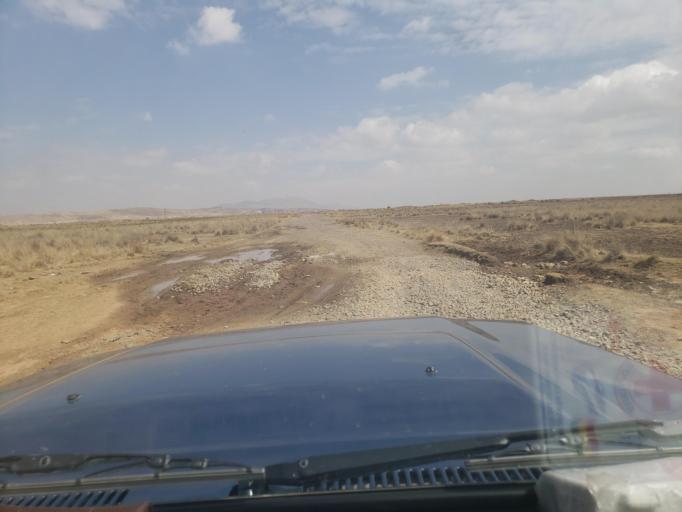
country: BO
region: La Paz
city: Batallas
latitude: -16.4097
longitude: -68.4431
